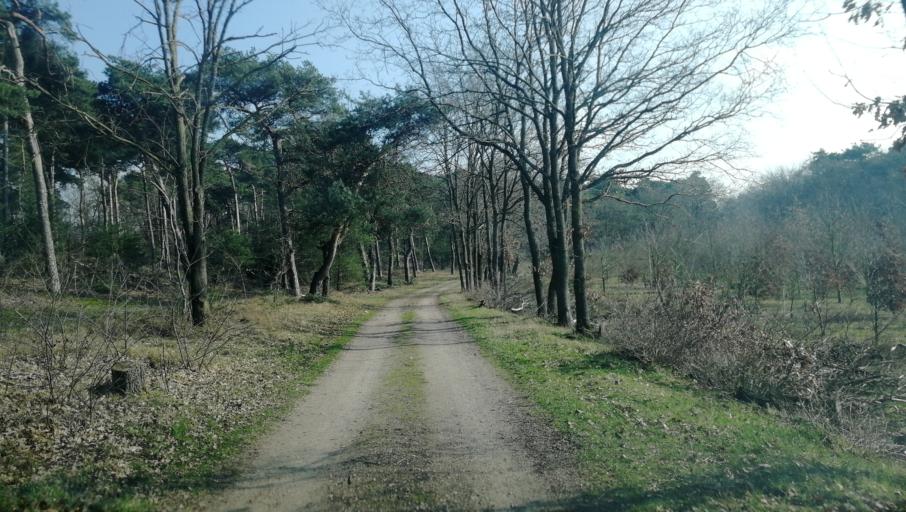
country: NL
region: Limburg
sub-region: Gemeente Venlo
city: Venlo
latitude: 51.3981
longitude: 6.1818
